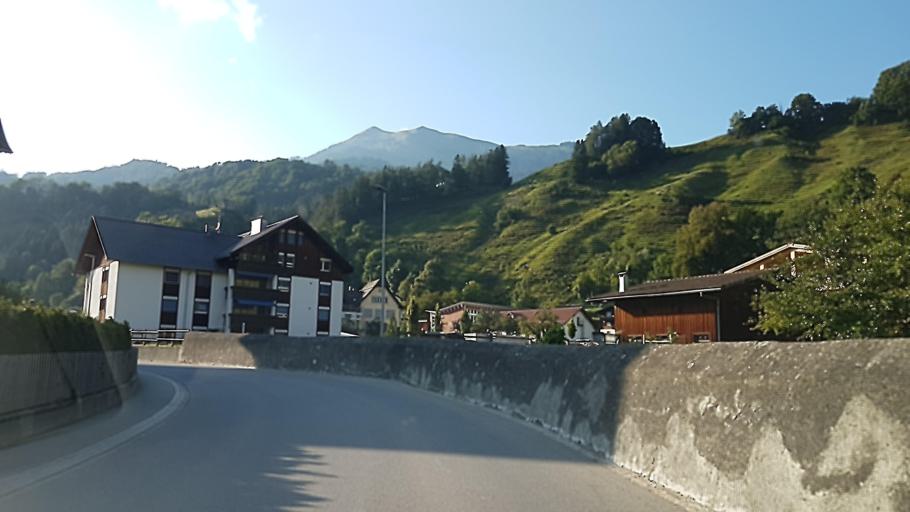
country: CH
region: Grisons
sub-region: Praettigau/Davos District
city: Grusch
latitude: 46.9811
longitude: 9.6497
